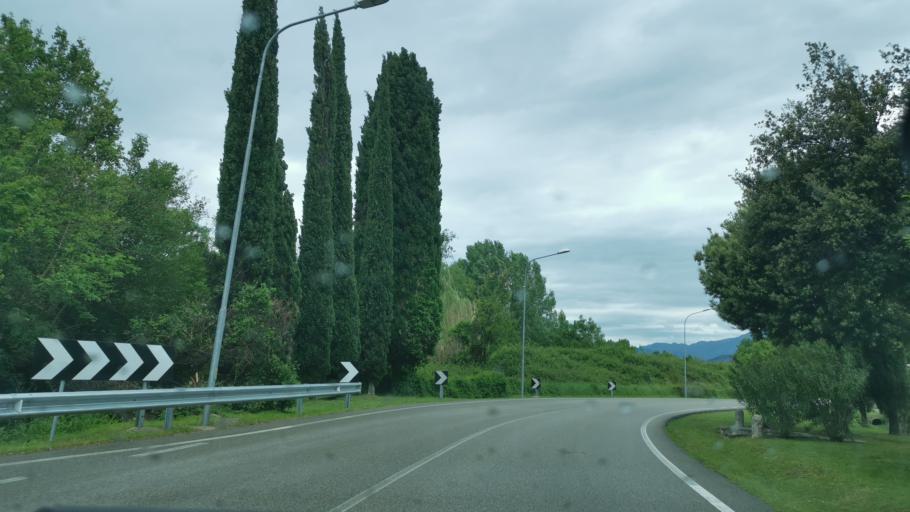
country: IT
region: Veneto
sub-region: Provincia di Verona
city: Bardolino
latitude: 45.5447
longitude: 10.7344
